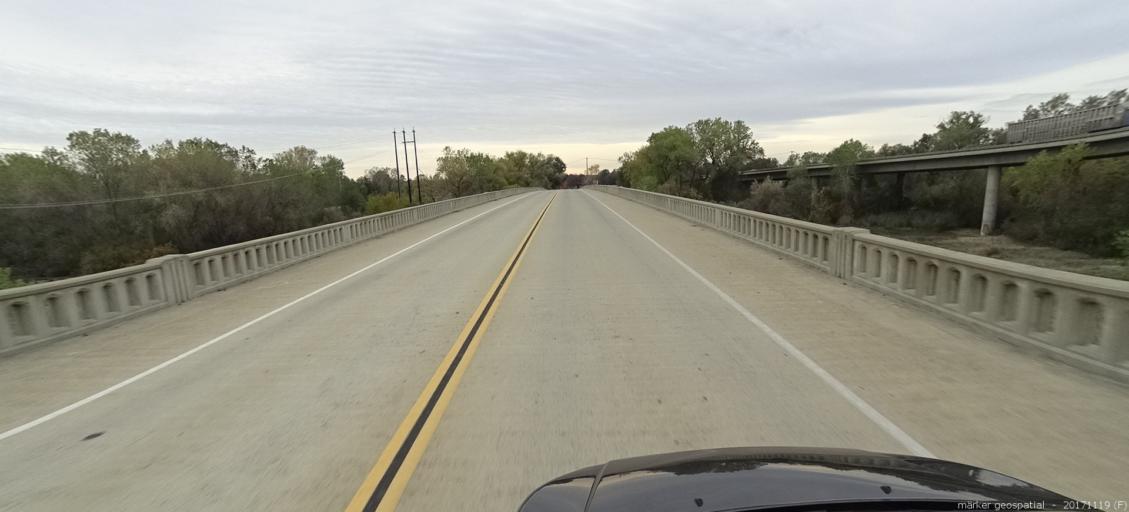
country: US
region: California
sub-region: Shasta County
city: Cottonwood
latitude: 40.3763
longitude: -122.2836
